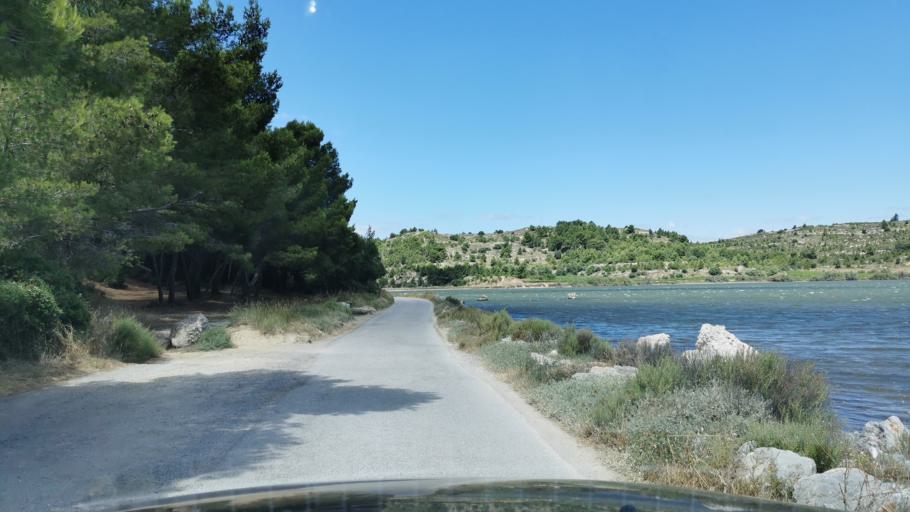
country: FR
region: Languedoc-Roussillon
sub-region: Departement de l'Aude
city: Peyriac-de-Mer
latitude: 43.0881
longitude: 2.9721
